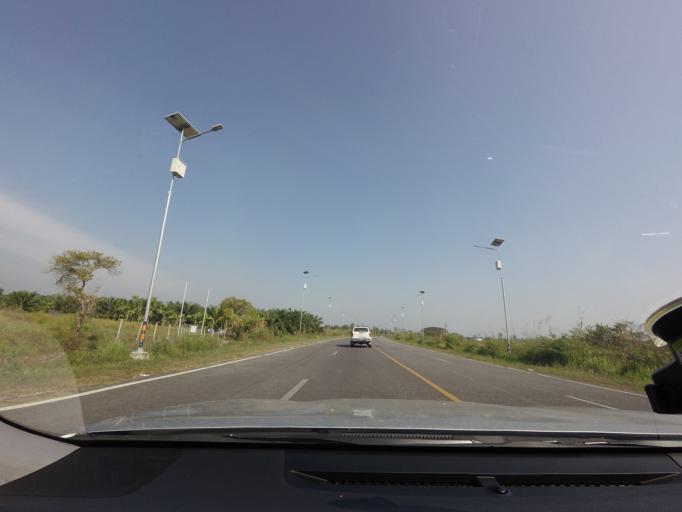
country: TH
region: Nakhon Si Thammarat
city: Nakhon Si Thammarat
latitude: 8.4822
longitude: 99.9765
